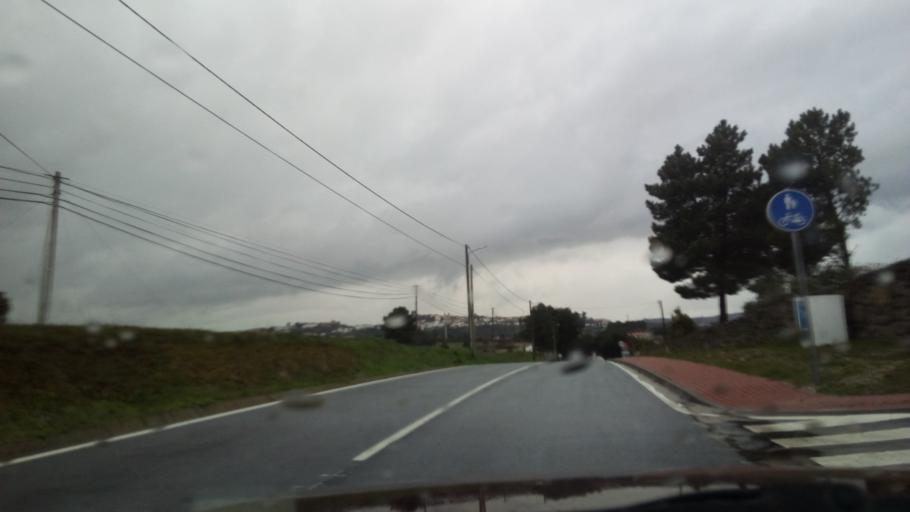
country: PT
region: Guarda
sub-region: Celorico da Beira
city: Celorico da Beira
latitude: 40.6396
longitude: -7.3667
